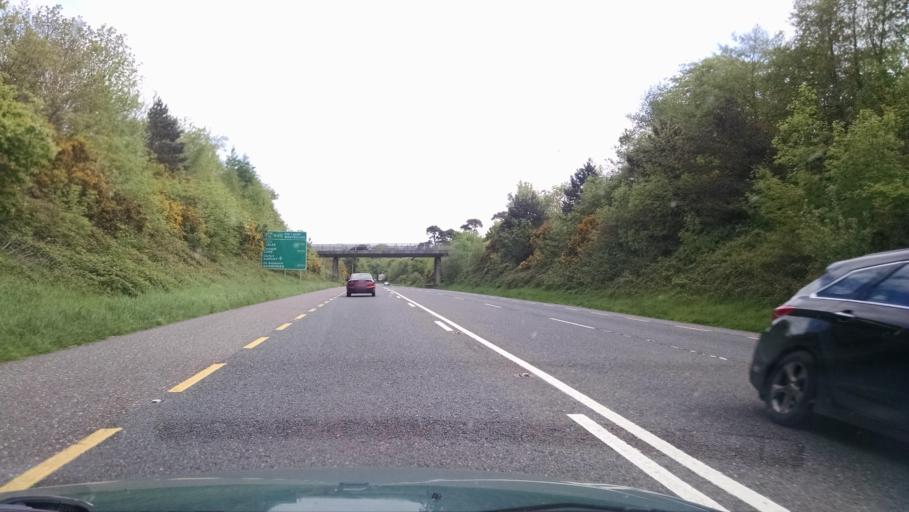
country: IE
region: Munster
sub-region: County Cork
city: Carrigaline
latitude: 51.8654
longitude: -8.4165
